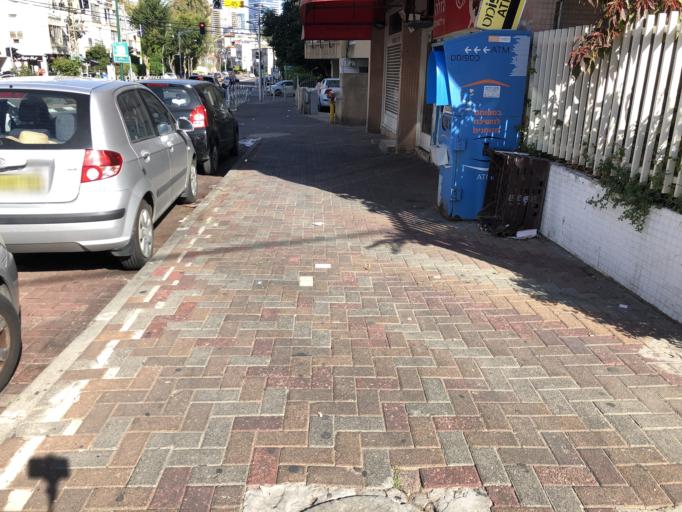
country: IL
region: Tel Aviv
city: Ramat Gan
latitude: 32.0832
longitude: 34.8213
